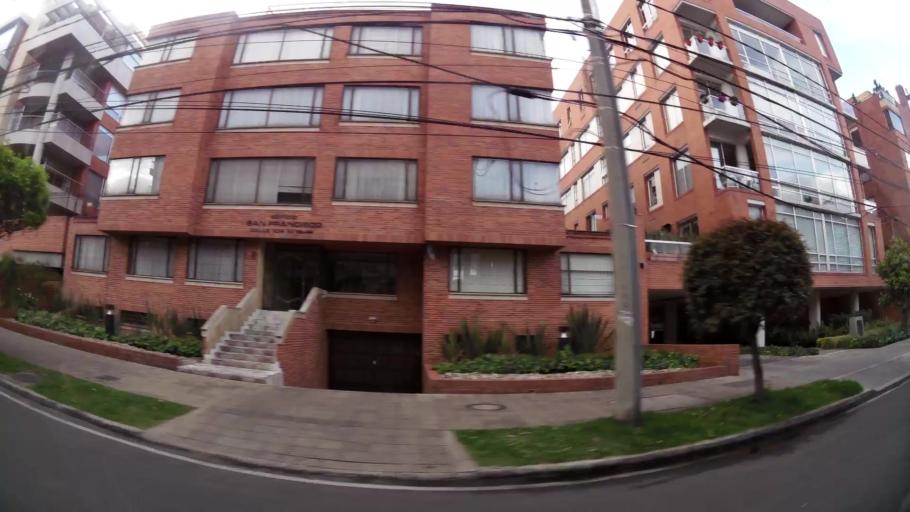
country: CO
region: Bogota D.C.
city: Barrio San Luis
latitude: 4.6907
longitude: -74.0528
